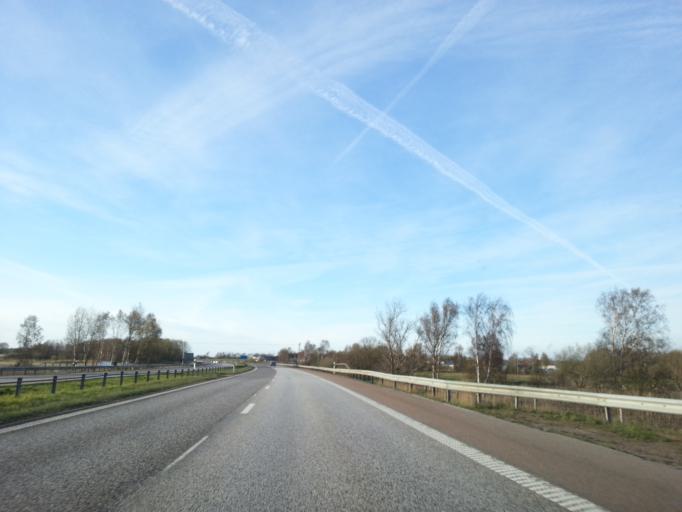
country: SE
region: Halland
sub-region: Laholms Kommun
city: Mellbystrand
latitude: 56.4397
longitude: 12.9543
